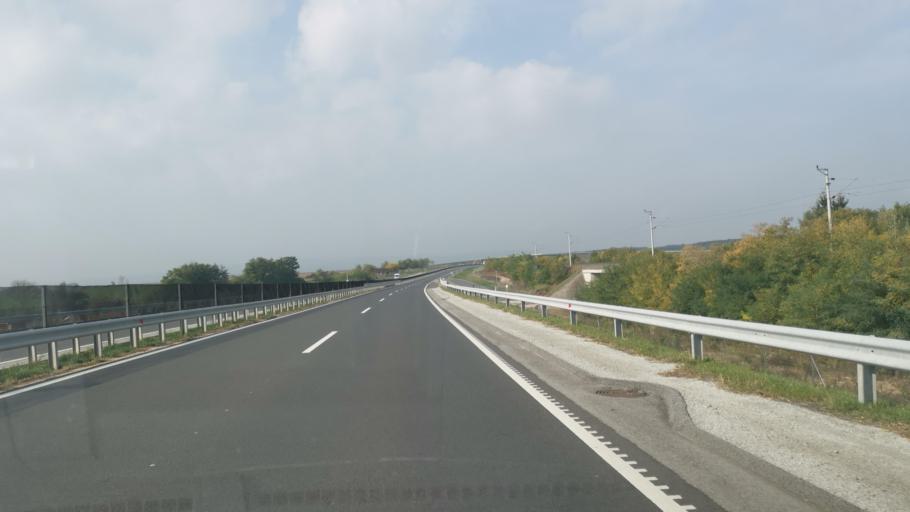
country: HU
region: Gyor-Moson-Sopron
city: Nagycenk
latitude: 47.6045
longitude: 16.6766
